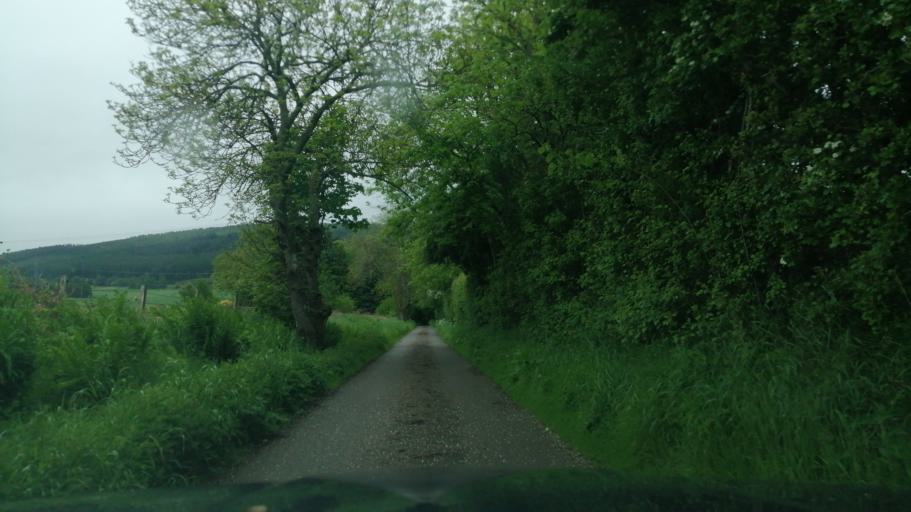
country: GB
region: Scotland
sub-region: Moray
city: Keith
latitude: 57.5530
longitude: -2.8714
